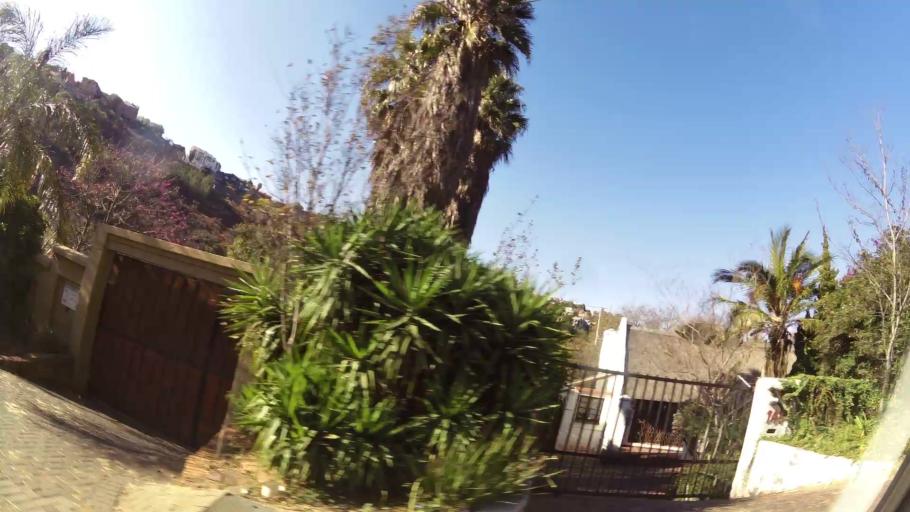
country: ZA
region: Gauteng
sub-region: City of Johannesburg Metropolitan Municipality
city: Johannesburg
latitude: -26.2761
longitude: 28.0505
